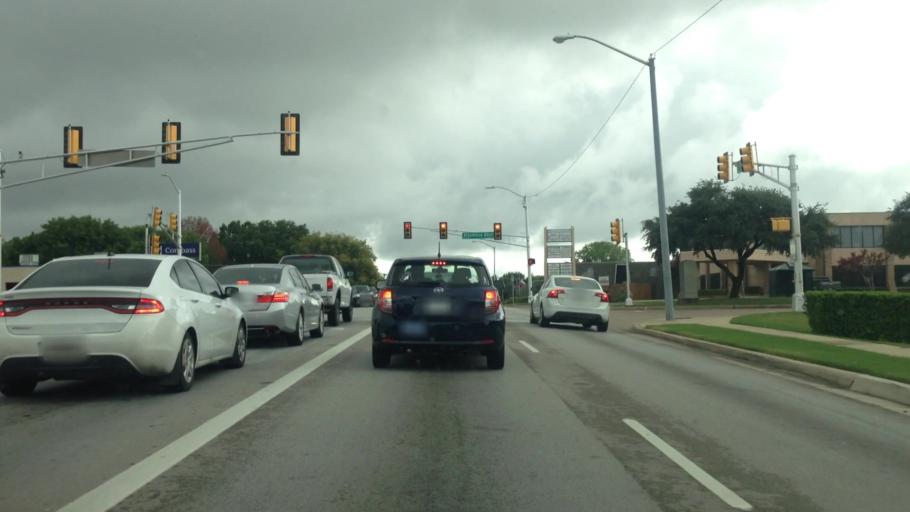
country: US
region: Texas
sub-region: Tarrant County
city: Edgecliff Village
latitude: 32.6485
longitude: -97.3960
